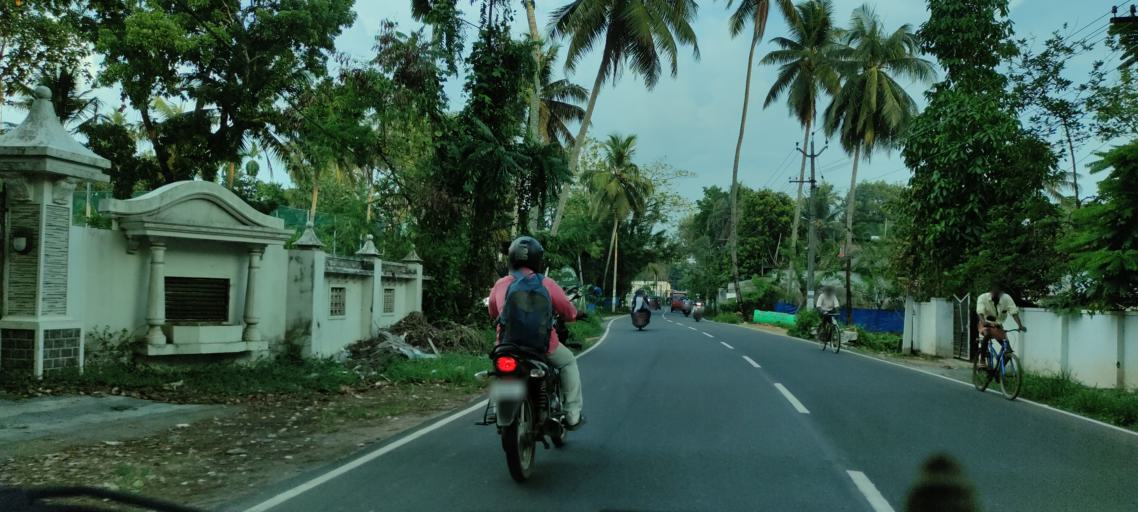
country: IN
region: Kerala
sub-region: Alappuzha
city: Arukutti
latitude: 9.8582
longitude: 76.3250
